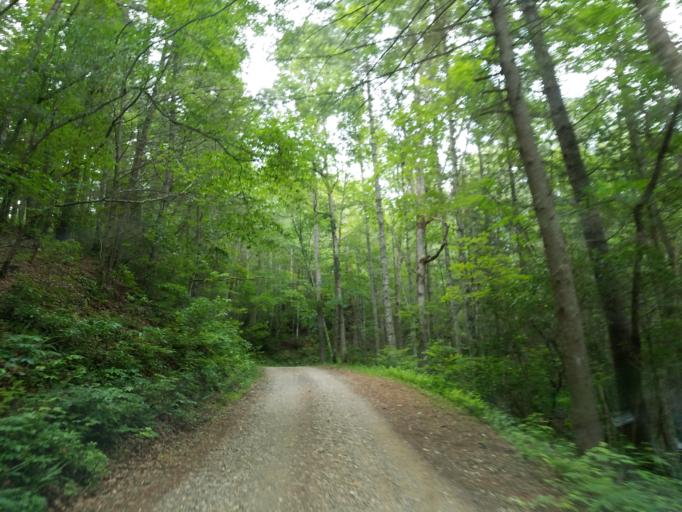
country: US
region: Georgia
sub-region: Union County
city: Blairsville
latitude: 34.7713
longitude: -84.0571
